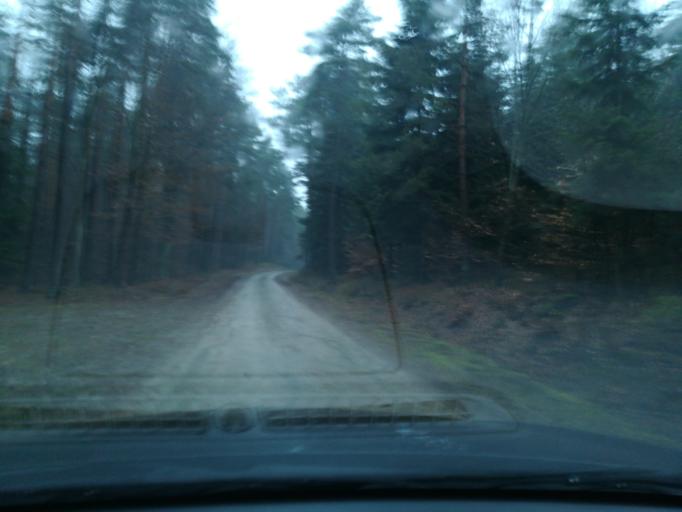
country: PL
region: Subcarpathian Voivodeship
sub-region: Powiat lancucki
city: Bialobrzegi
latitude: 50.1267
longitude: 22.3651
